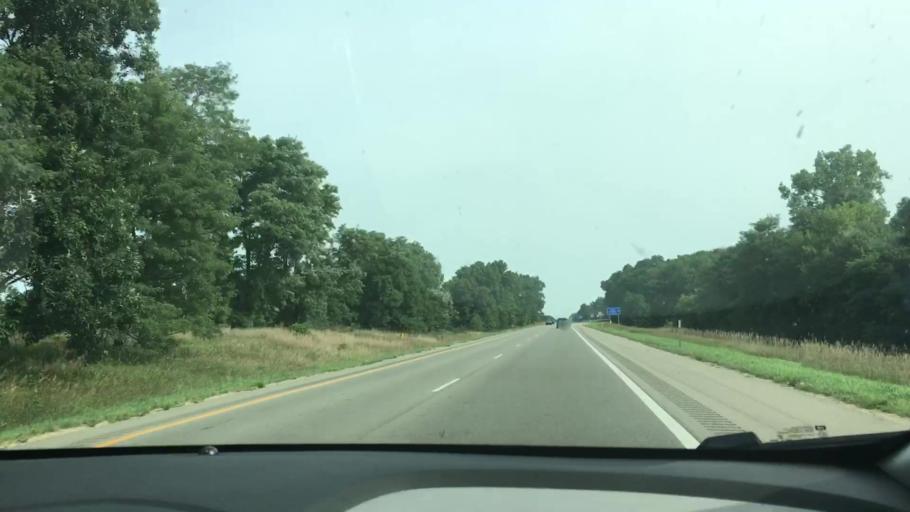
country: US
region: Michigan
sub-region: Kalamazoo County
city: Schoolcraft
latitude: 42.1662
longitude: -85.6444
